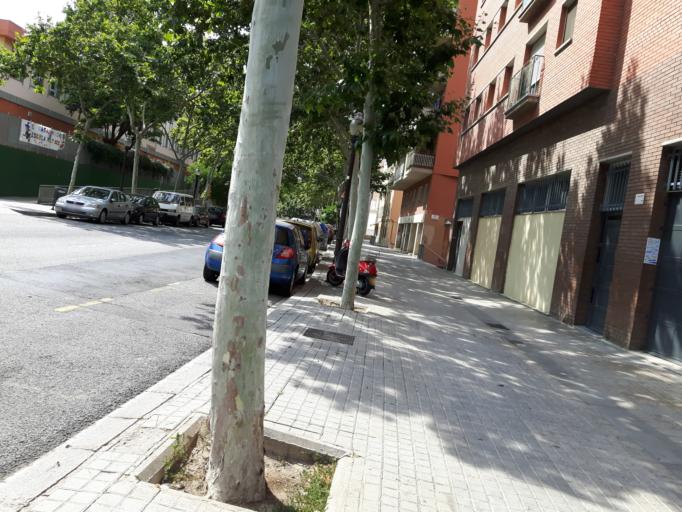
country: ES
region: Catalonia
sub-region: Provincia de Barcelona
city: Sants-Montjuic
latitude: 41.3706
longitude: 2.1654
